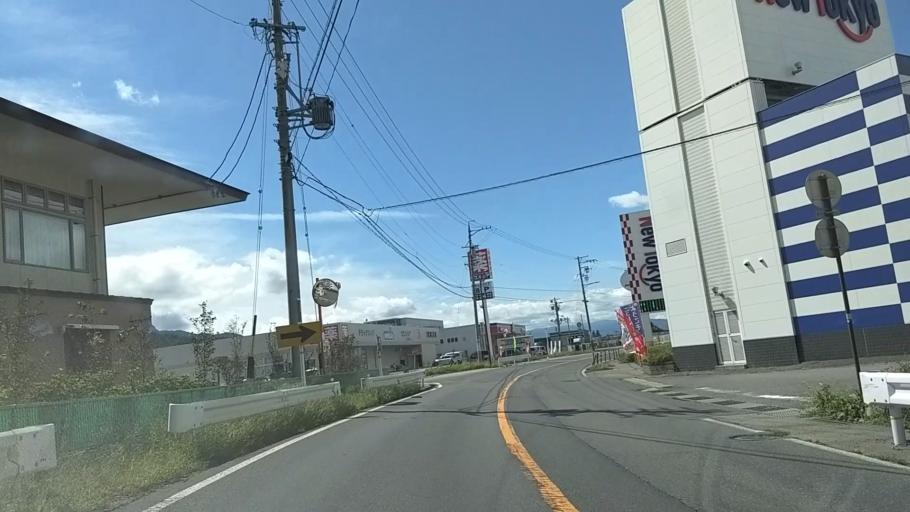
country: JP
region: Nagano
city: Suzaka
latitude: 36.6333
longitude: 138.2717
